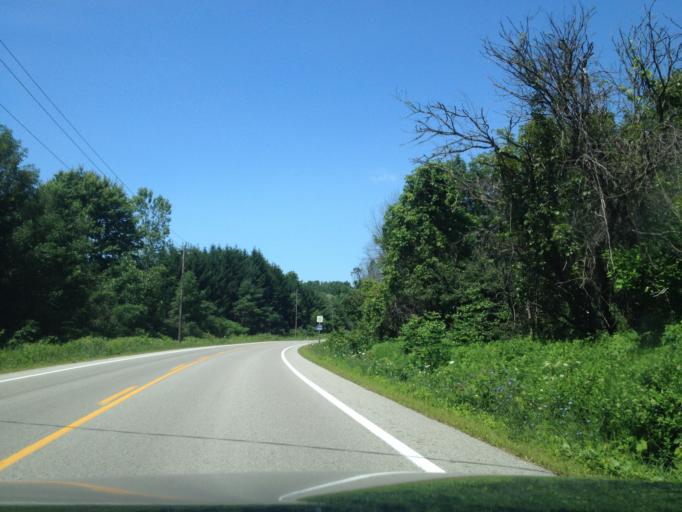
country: CA
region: Ontario
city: Norfolk County
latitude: 42.5852
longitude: -80.6165
